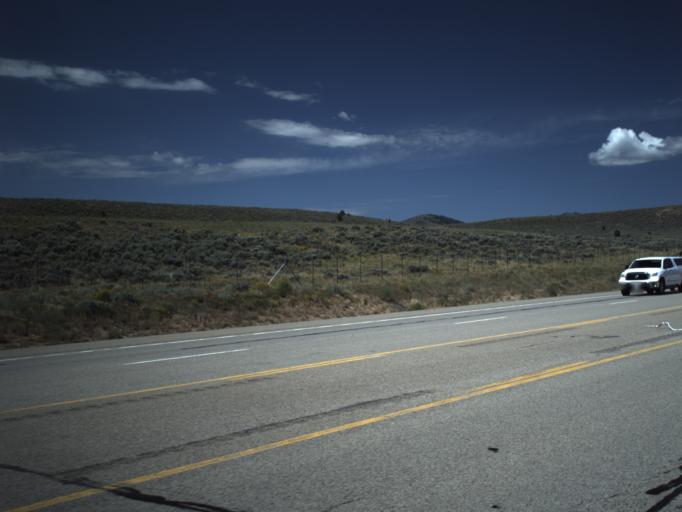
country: US
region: Utah
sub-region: Carbon County
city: Helper
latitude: 39.8421
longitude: -110.9912
